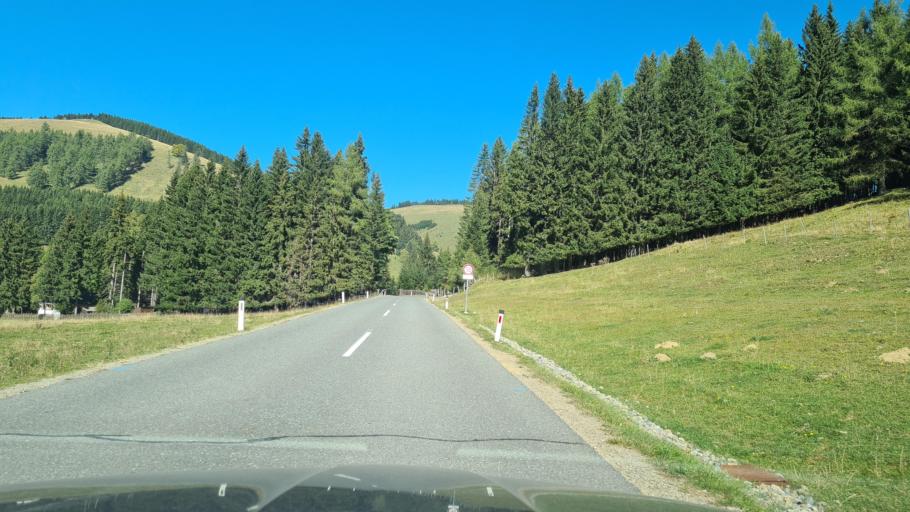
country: AT
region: Styria
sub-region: Politischer Bezirk Weiz
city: Passail
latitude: 47.3460
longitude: 15.4815
